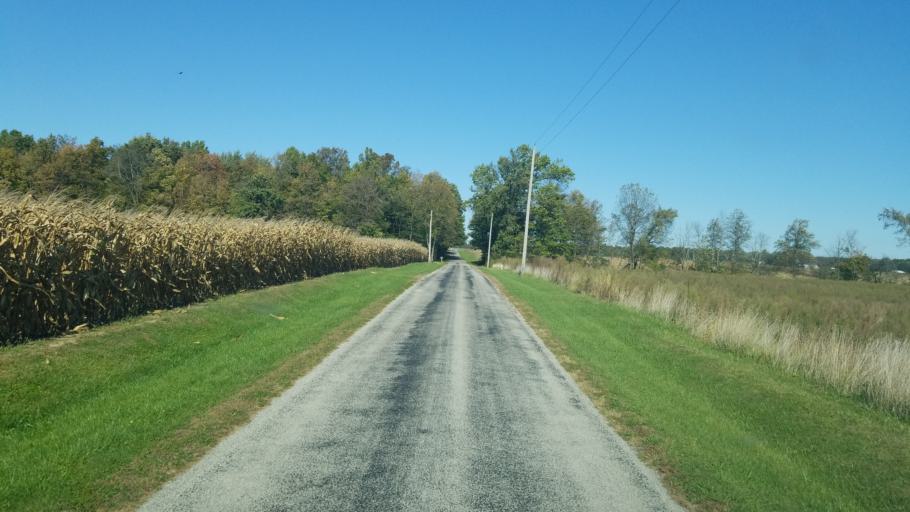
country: US
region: Ohio
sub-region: Huron County
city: Willard
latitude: 41.0369
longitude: -82.7650
